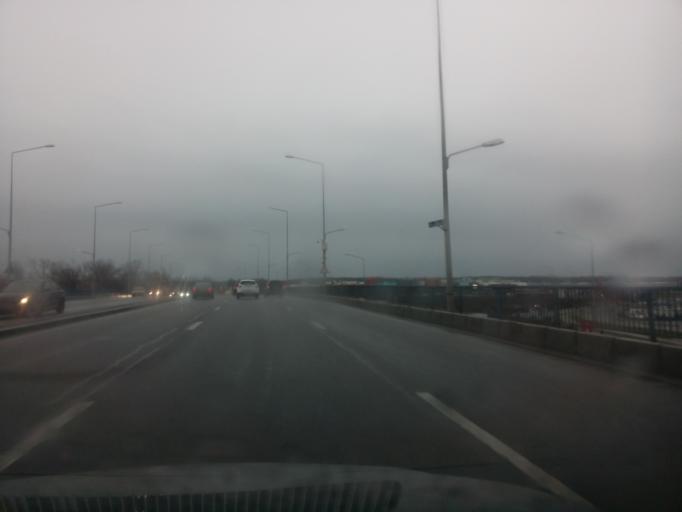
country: RO
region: Ilfov
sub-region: Comuna Otopeni
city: Otopeni
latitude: 44.5053
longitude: 26.0817
